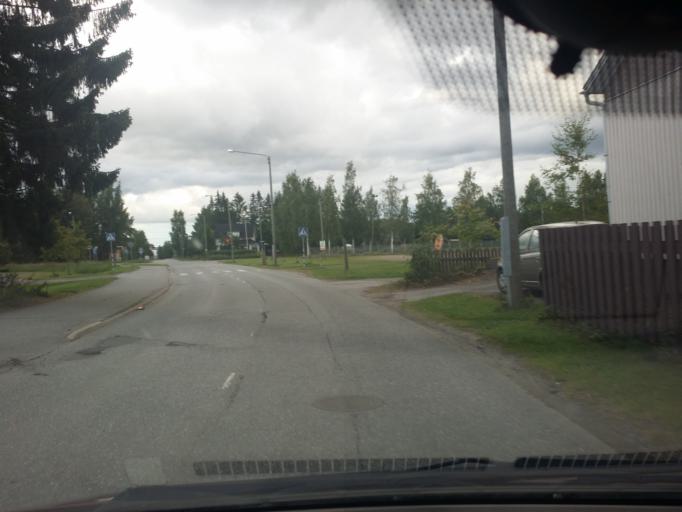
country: FI
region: Satakunta
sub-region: Pori
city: Pori
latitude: 61.5043
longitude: 21.8044
